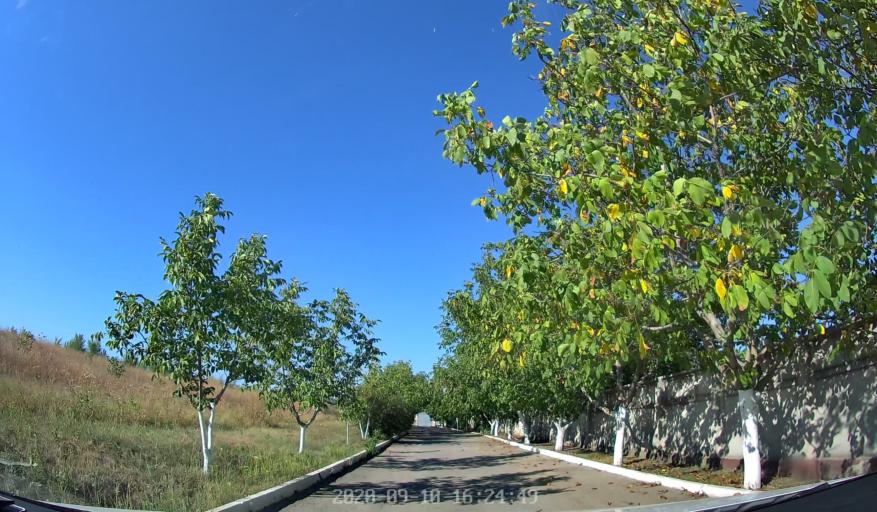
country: MD
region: Chisinau
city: Stauceni
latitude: 47.0540
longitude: 28.9206
